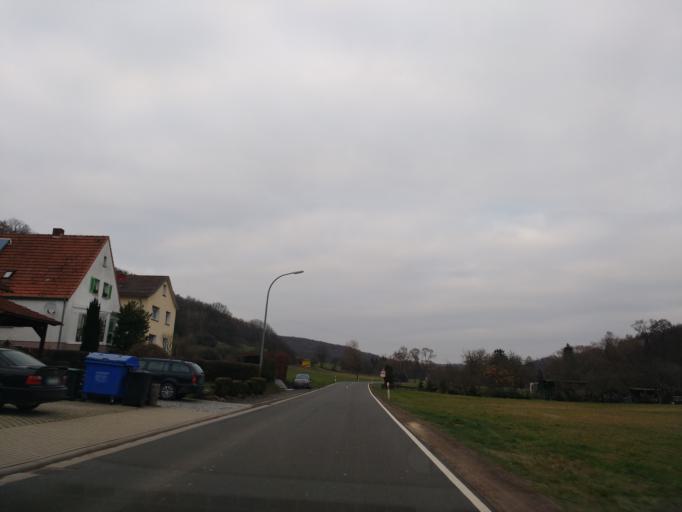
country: DE
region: Hesse
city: Bebra
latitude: 50.9973
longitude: 9.7664
